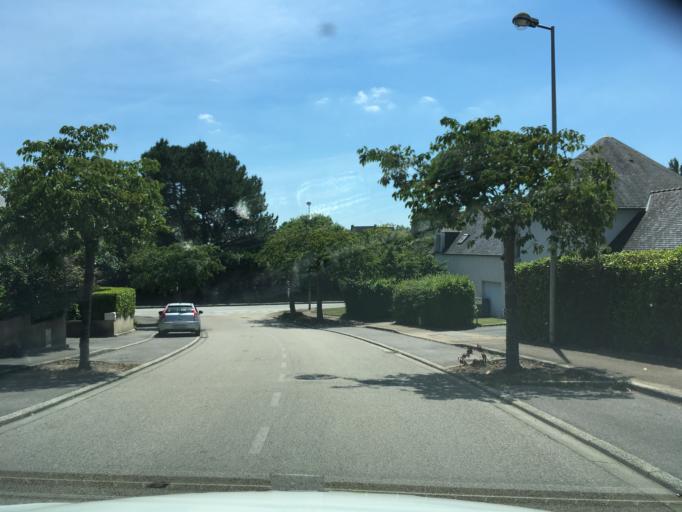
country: FR
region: Brittany
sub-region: Departement du Finistere
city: Quimper
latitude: 47.9958
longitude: -4.1377
